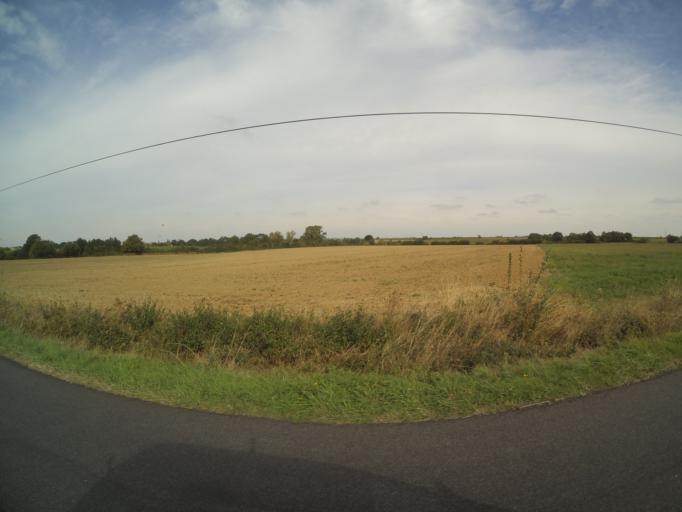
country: FR
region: Pays de la Loire
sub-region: Departement de Maine-et-Loire
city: Martigne-Briand
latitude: 47.2079
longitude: -0.4764
